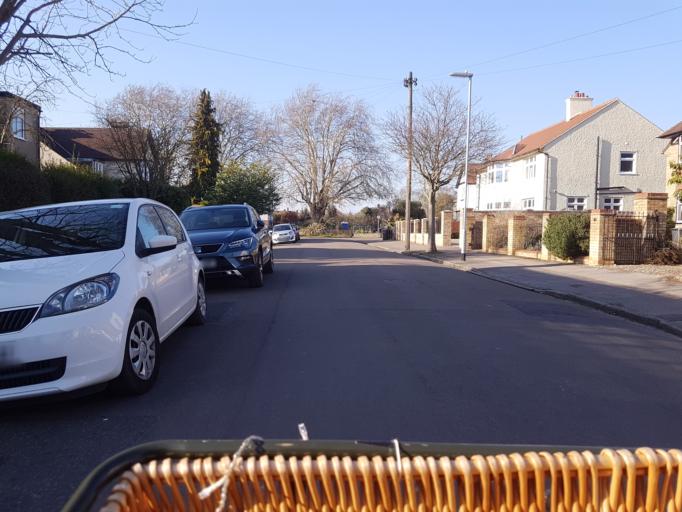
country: GB
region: England
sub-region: Cambridgeshire
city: Cambridge
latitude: 52.2205
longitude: 0.1303
